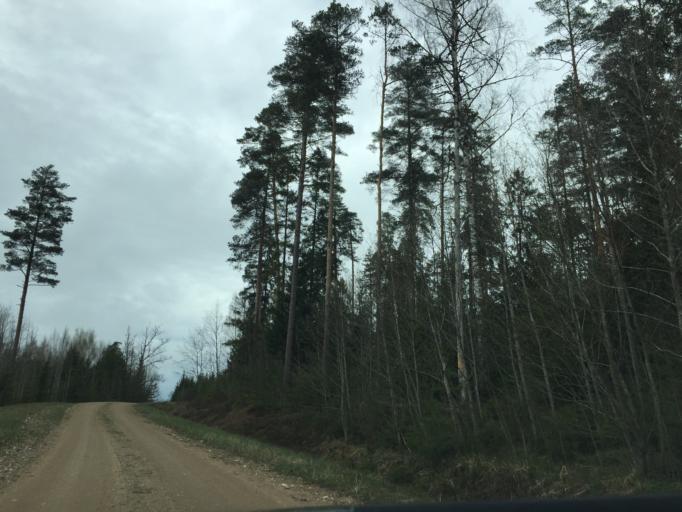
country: LV
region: Malpils
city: Malpils
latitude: 57.0448
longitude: 25.0774
